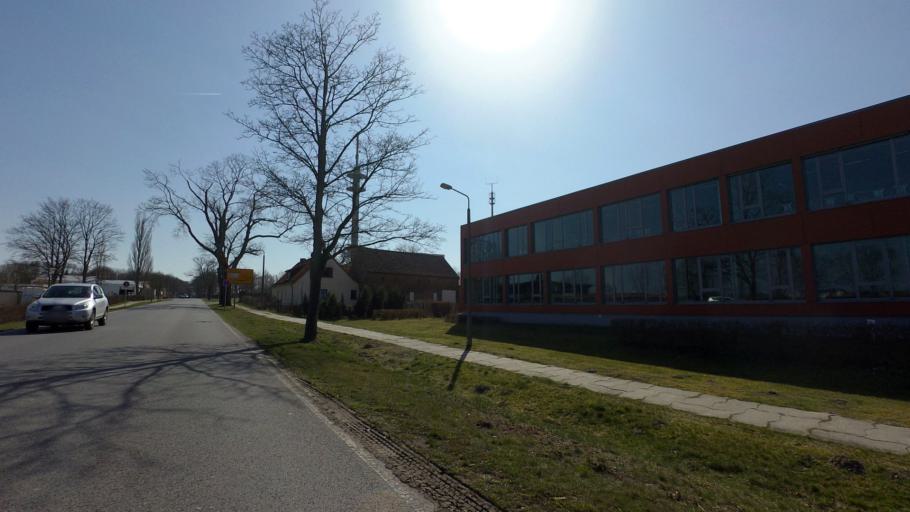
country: DE
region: Brandenburg
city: Gransee
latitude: 53.0006
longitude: 13.1541
